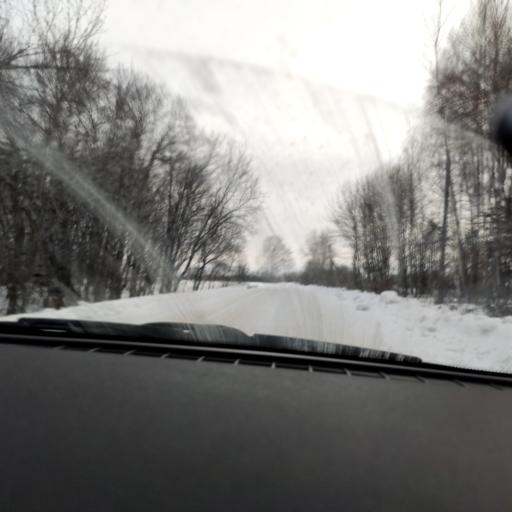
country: RU
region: Bashkortostan
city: Iglino
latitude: 54.7669
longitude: 56.5337
